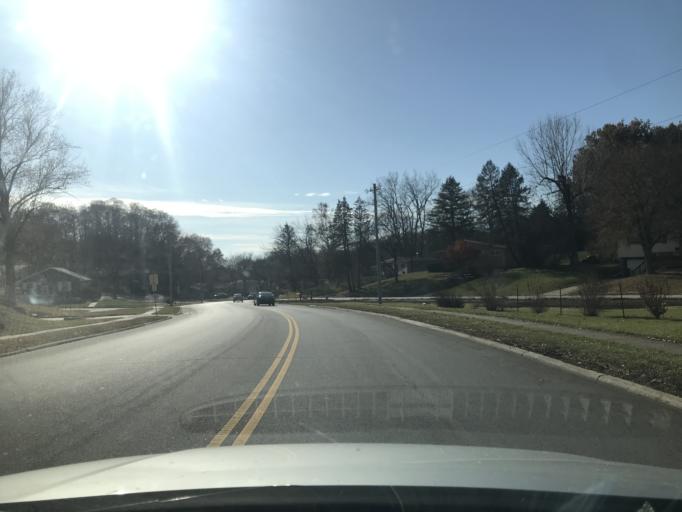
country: US
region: Iowa
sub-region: Scott County
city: Davenport
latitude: 41.5283
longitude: -90.6157
